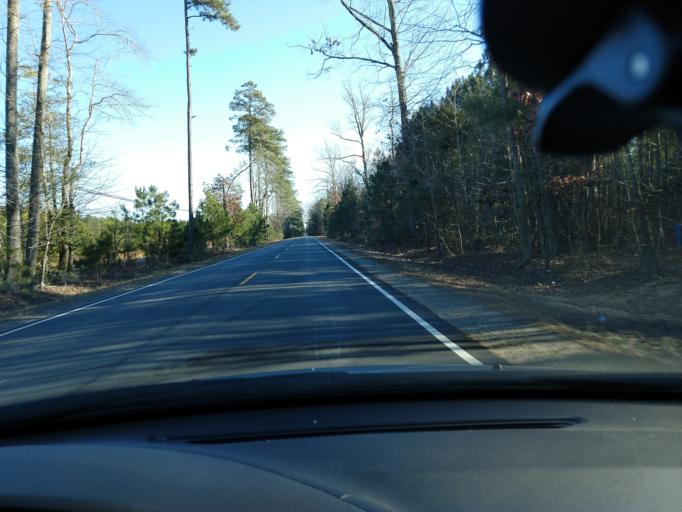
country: US
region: Virginia
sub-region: Surry County
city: Surry
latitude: 37.2760
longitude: -76.9099
